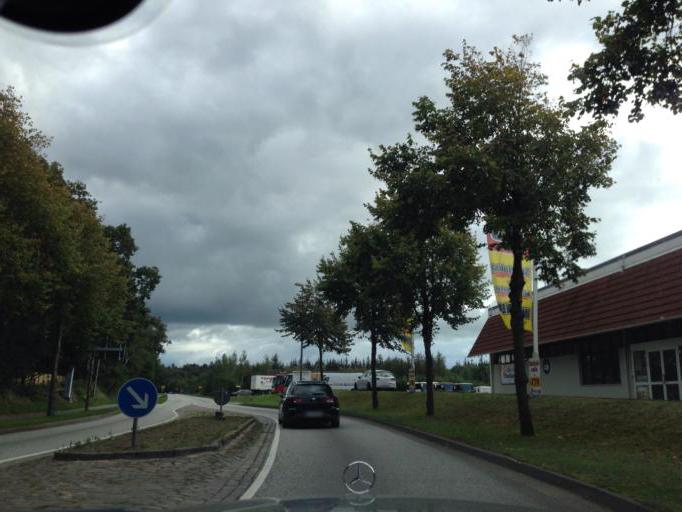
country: DE
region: Schleswig-Holstein
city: Leck
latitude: 54.7634
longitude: 8.9811
